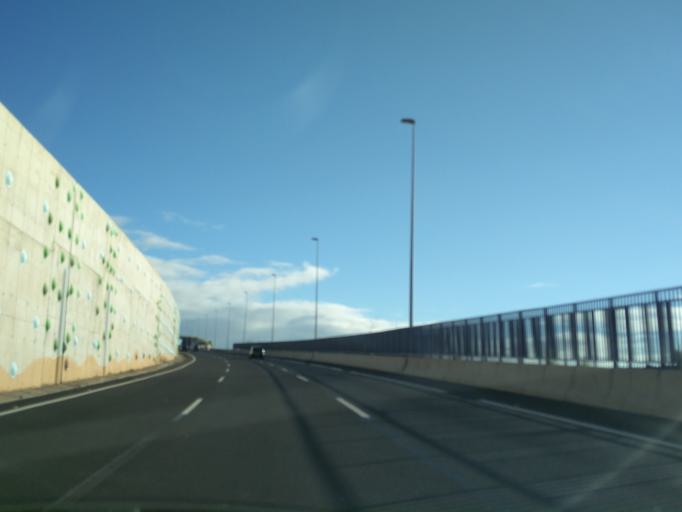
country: ES
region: Canary Islands
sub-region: Provincia de Santa Cruz de Tenerife
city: Candelaria
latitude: 28.3855
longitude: -16.3526
